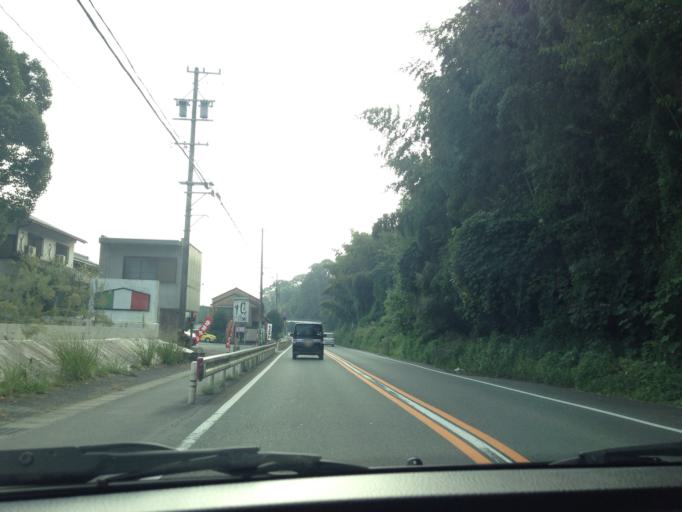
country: JP
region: Aichi
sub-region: Tokai-shi
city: Toyokawa
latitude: 34.8664
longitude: 137.4381
